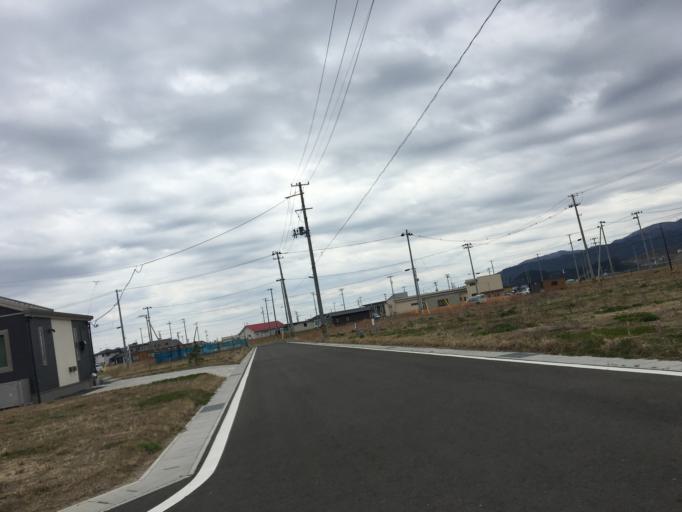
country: JP
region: Iwate
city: Ofunato
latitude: 39.0198
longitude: 141.6238
